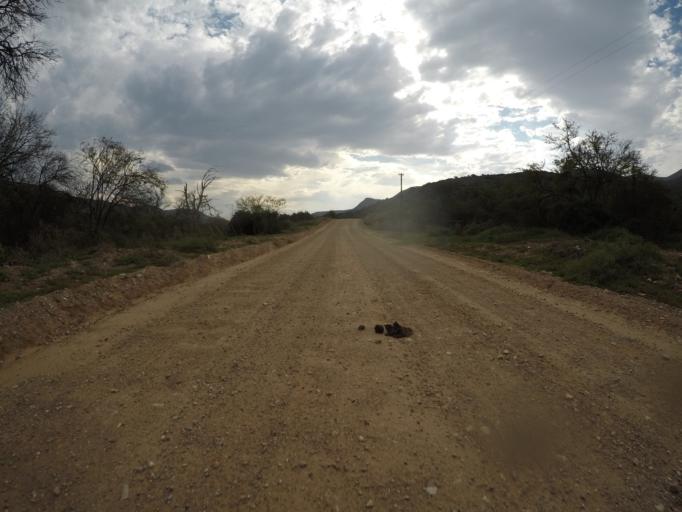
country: ZA
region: Eastern Cape
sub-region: Cacadu District Municipality
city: Kareedouw
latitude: -33.5892
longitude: 24.1737
